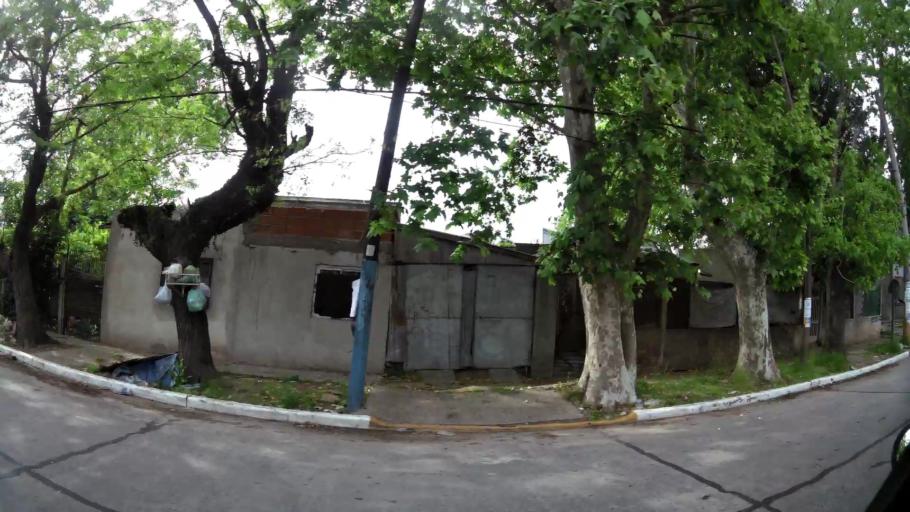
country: AR
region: Buenos Aires
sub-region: Partido de Quilmes
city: Quilmes
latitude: -34.7209
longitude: -58.2424
